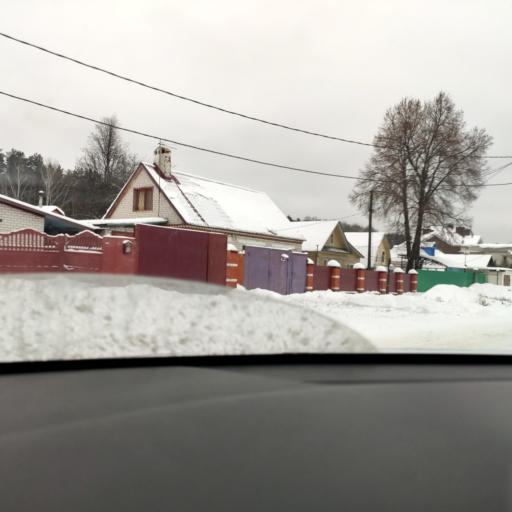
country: RU
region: Tatarstan
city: Osinovo
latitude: 55.8294
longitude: 48.8732
